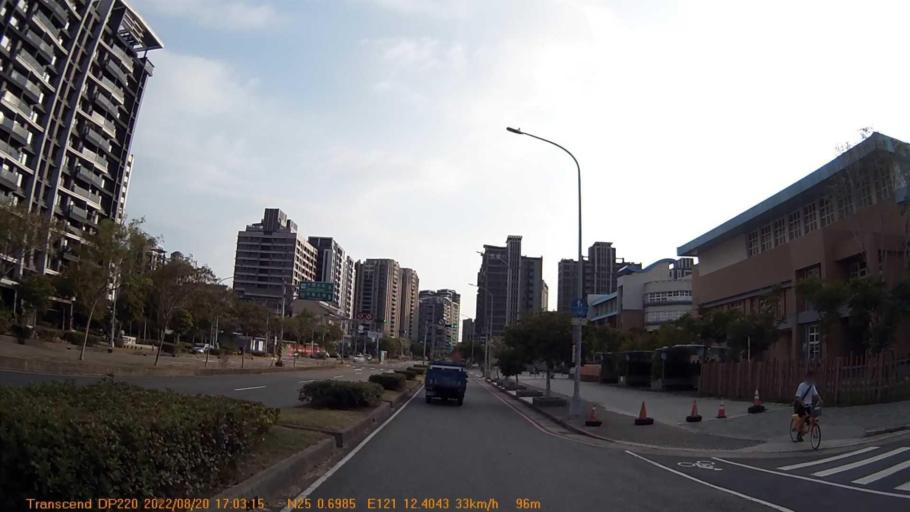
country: TW
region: Taiwan
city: Taoyuan City
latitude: 25.0114
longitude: 121.2065
